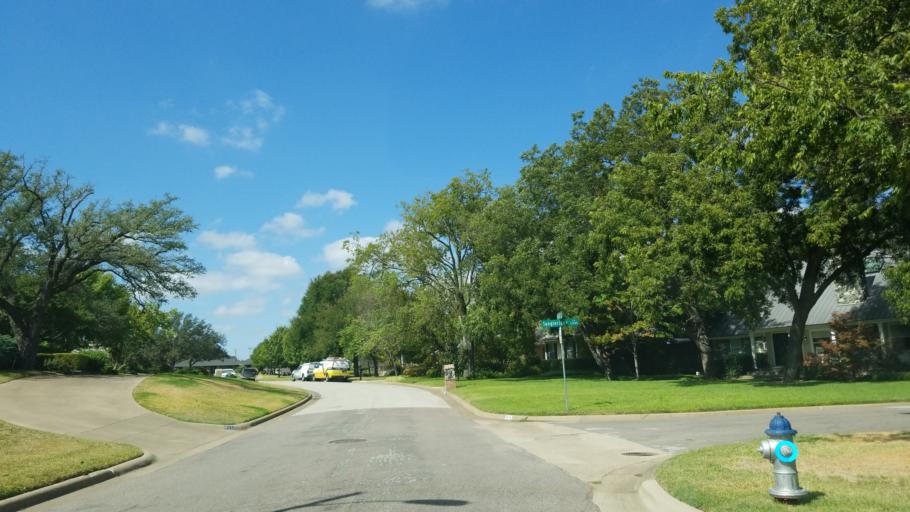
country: US
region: Texas
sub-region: Dallas County
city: Addison
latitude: 32.9312
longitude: -96.7996
